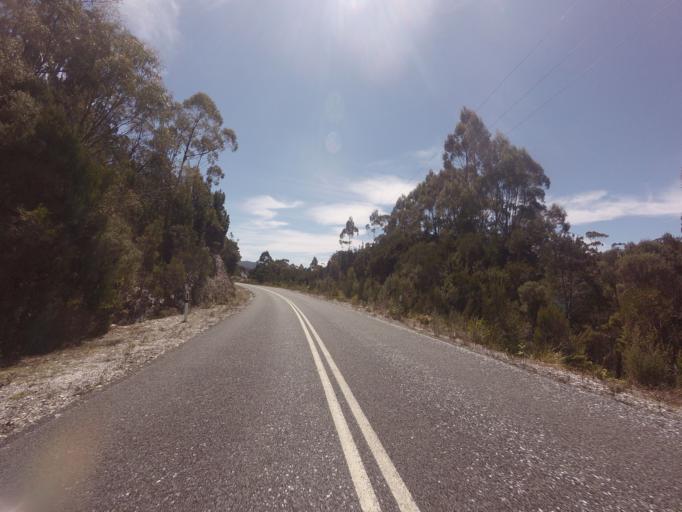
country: AU
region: Tasmania
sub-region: West Coast
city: Queenstown
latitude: -42.7614
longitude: 146.0048
